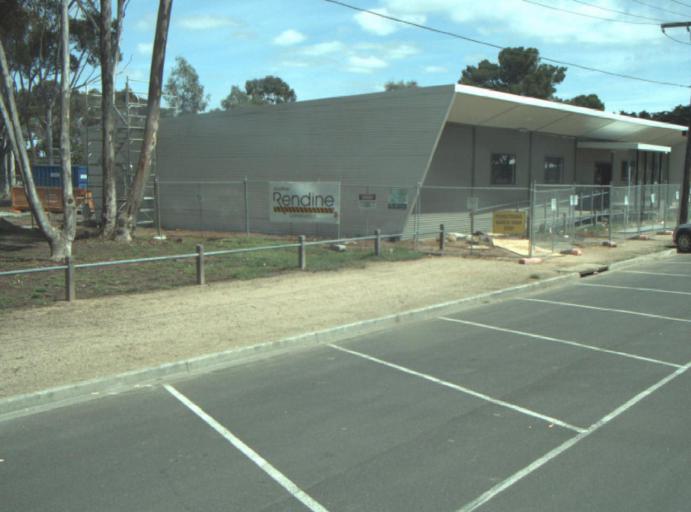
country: AU
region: Victoria
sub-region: Greater Geelong
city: Lara
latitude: -38.0223
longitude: 144.4115
